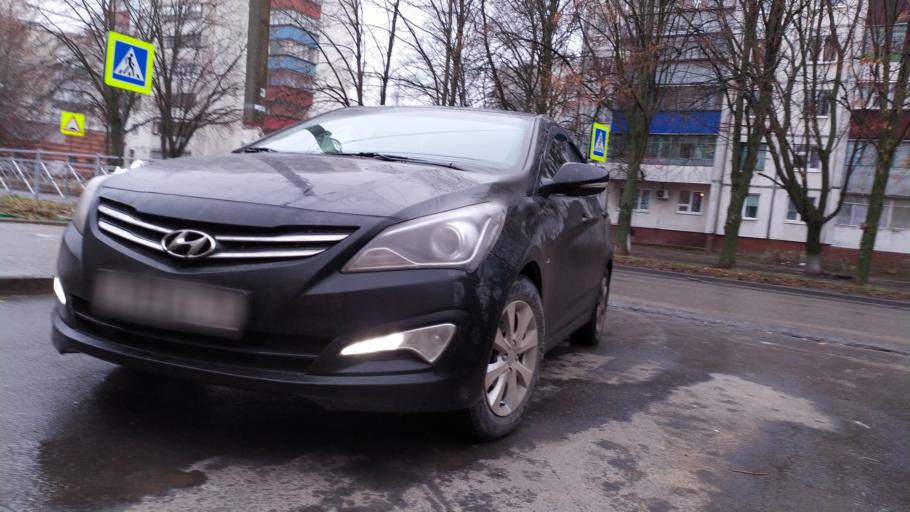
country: RU
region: Kursk
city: Kursk
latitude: 51.7425
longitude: 36.1346
